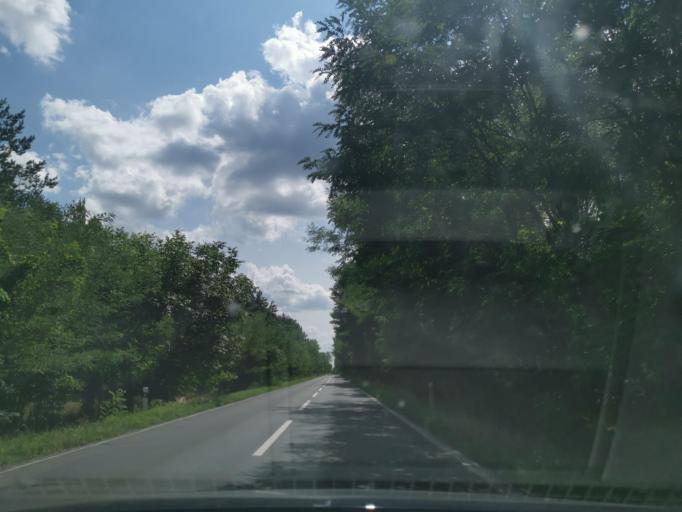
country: AT
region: Lower Austria
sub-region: Politischer Bezirk Ganserndorf
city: Drosing
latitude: 48.5643
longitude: 16.9902
